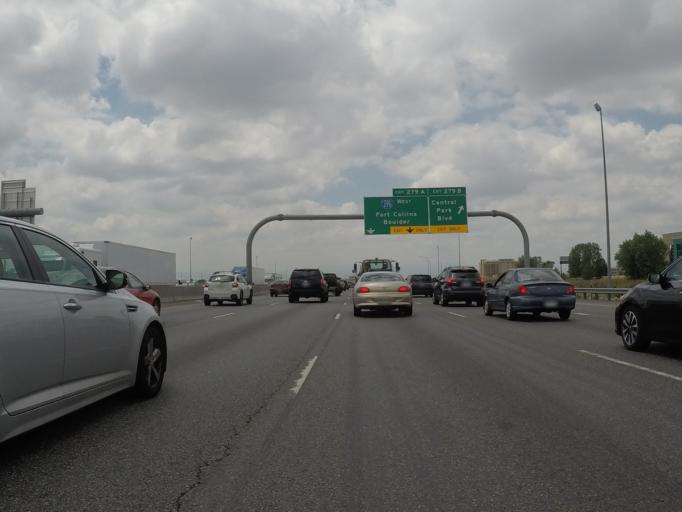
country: US
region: Colorado
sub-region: Adams County
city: Aurora
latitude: 39.7765
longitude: -104.8730
